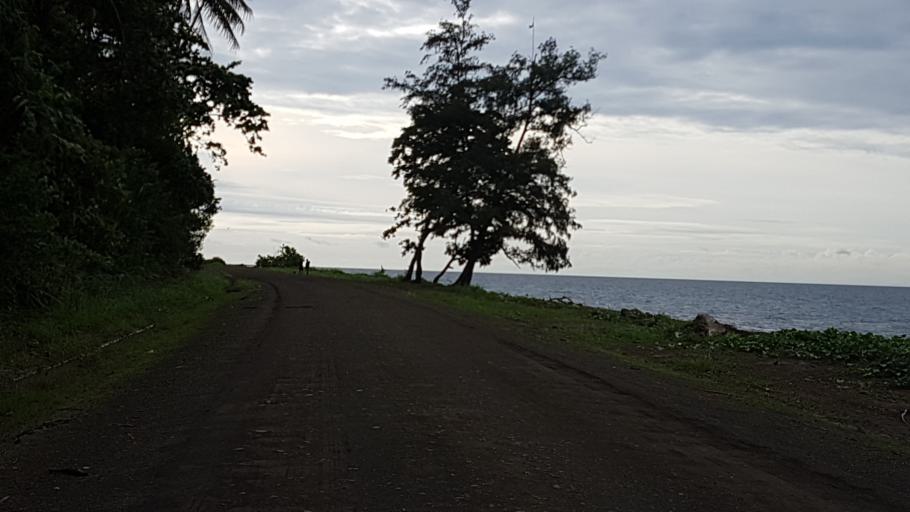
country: PG
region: Milne Bay
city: Alotau
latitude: -10.3161
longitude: 150.7148
